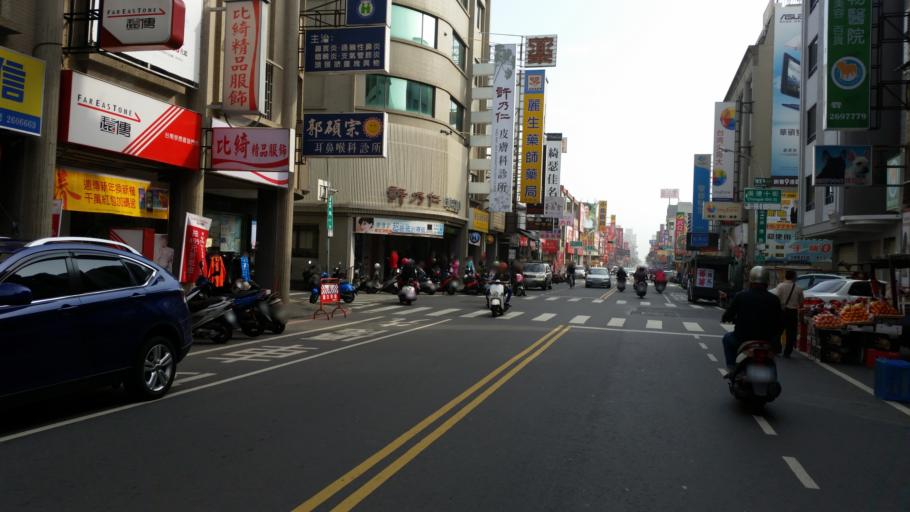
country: TW
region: Taiwan
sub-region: Tainan
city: Tainan
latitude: 22.9733
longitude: 120.2275
